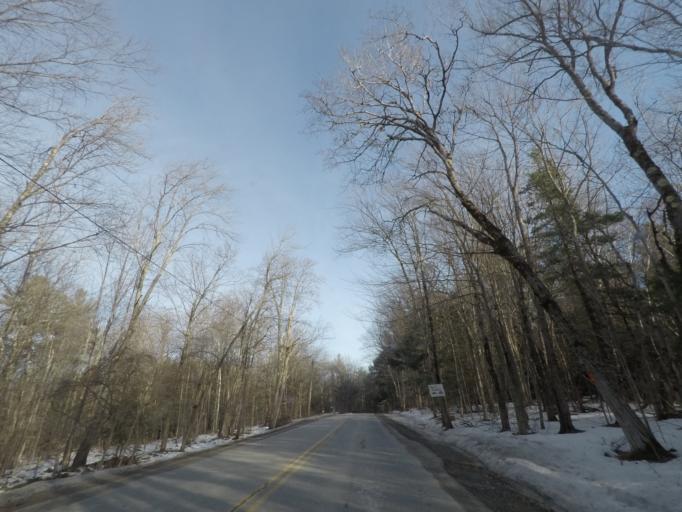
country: US
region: New York
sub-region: Rensselaer County
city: Poestenkill
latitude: 42.7443
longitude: -73.4091
